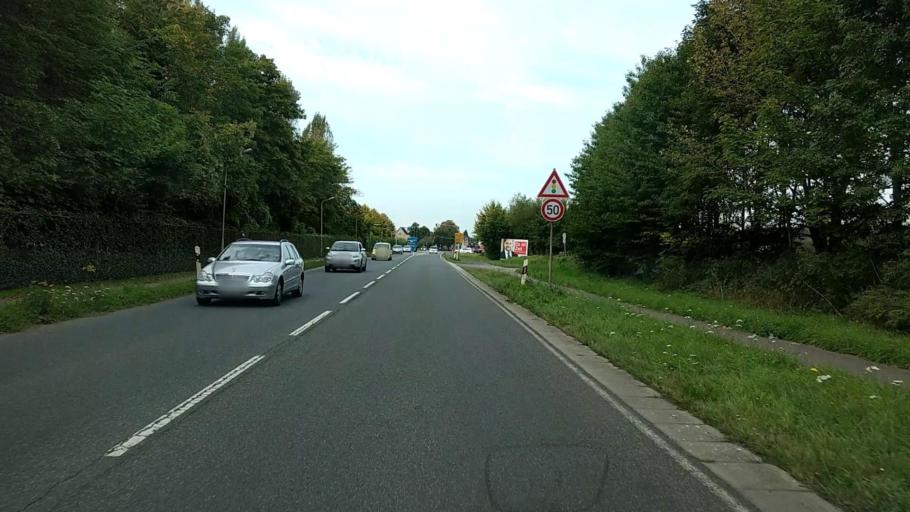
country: DE
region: North Rhine-Westphalia
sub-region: Regierungsbezirk Koln
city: Bergheim
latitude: 50.9480
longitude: 6.6629
